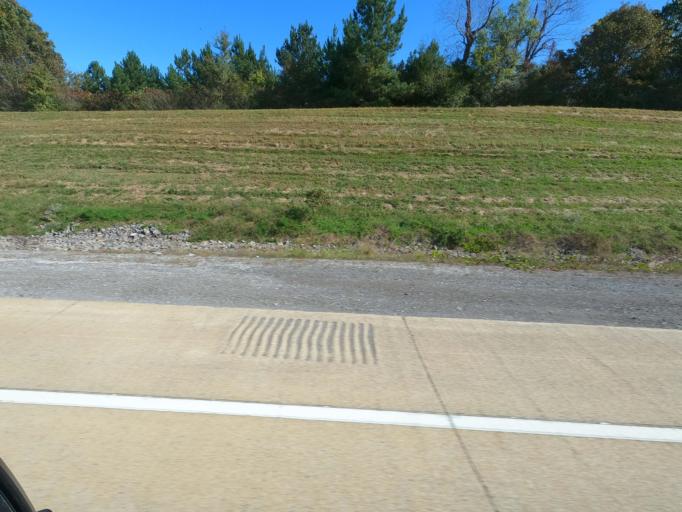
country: US
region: Tennessee
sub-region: Williamson County
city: Fairview
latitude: 35.9382
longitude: -87.1876
